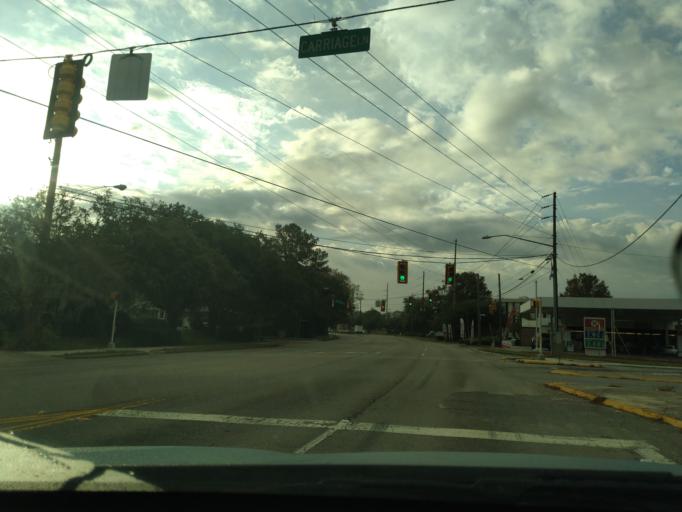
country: US
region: South Carolina
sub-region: Charleston County
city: North Charleston
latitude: 32.7992
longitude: -79.9964
